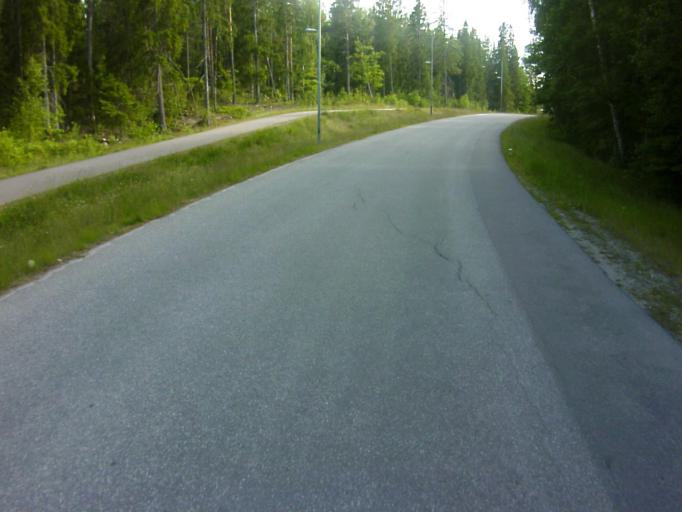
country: SE
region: Soedermanland
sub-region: Eskilstuna Kommun
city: Eskilstuna
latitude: 59.3527
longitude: 16.5123
